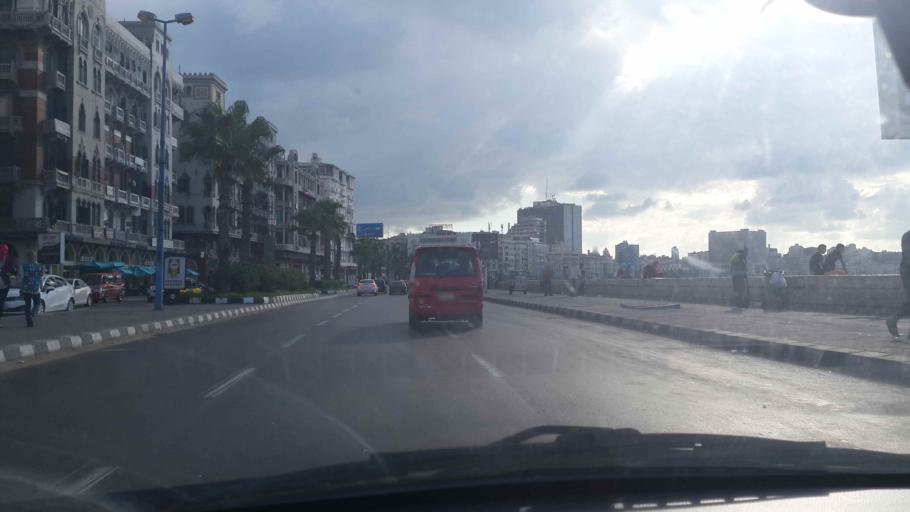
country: EG
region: Alexandria
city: Alexandria
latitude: 31.2034
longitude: 29.9024
